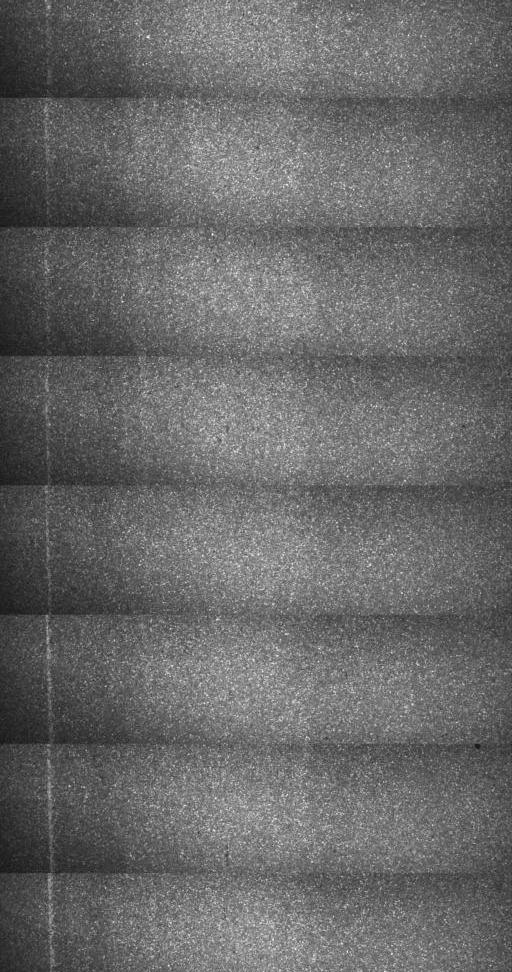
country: US
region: Vermont
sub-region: Caledonia County
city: Hardwick
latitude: 44.5417
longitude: -72.4557
